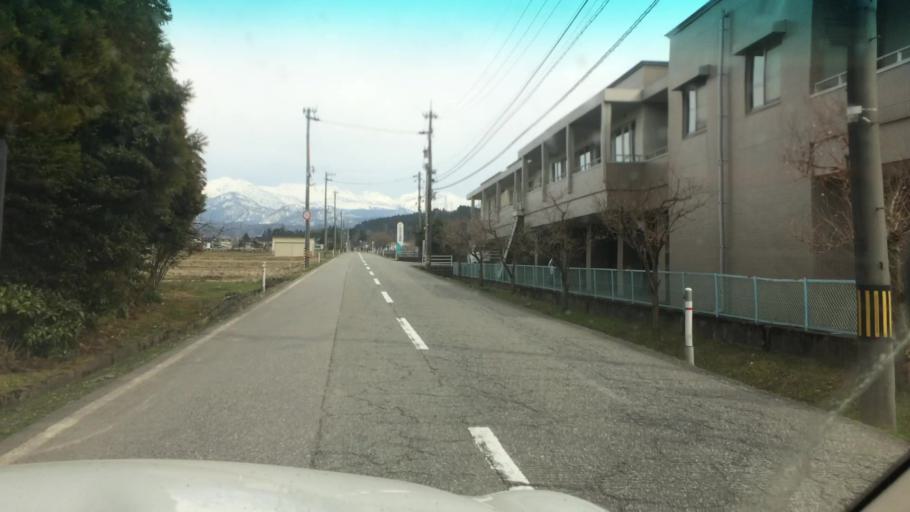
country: JP
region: Toyama
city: Toyama-shi
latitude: 36.6105
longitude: 137.2795
